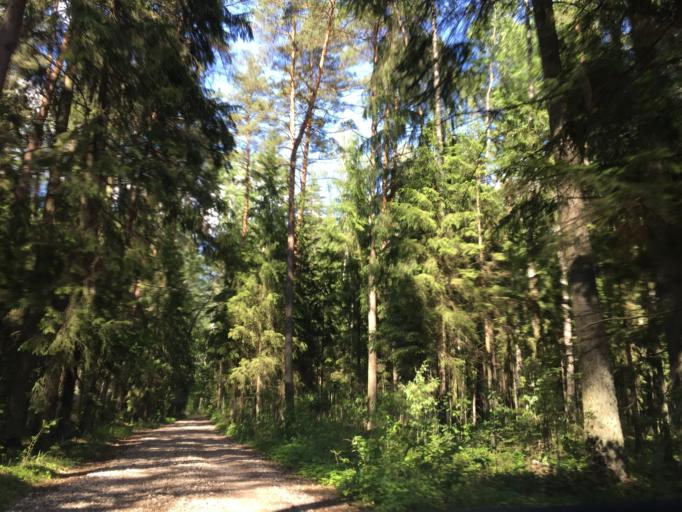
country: LV
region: Engure
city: Smarde
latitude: 56.8188
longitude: 23.3902
